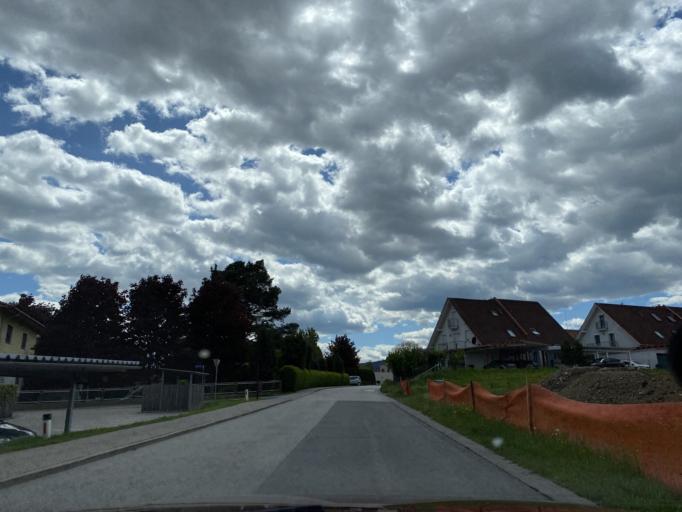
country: AT
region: Carinthia
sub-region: Politischer Bezirk Wolfsberg
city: Wolfsberg
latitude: 46.8285
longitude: 14.8330
